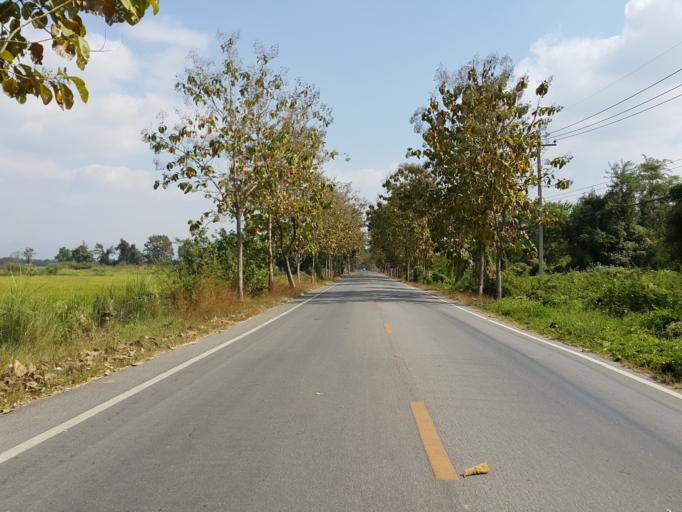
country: TH
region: Chiang Mai
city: San Kamphaeng
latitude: 18.7274
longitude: 99.1423
